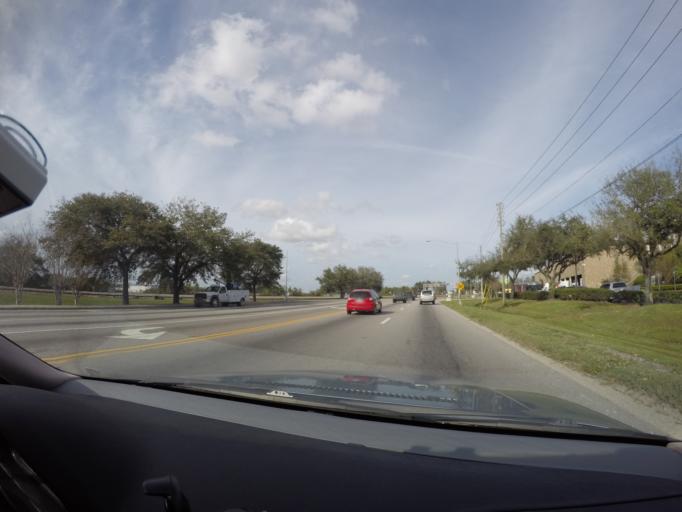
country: US
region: Florida
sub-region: Orange County
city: Taft
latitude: 28.4366
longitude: -81.3674
